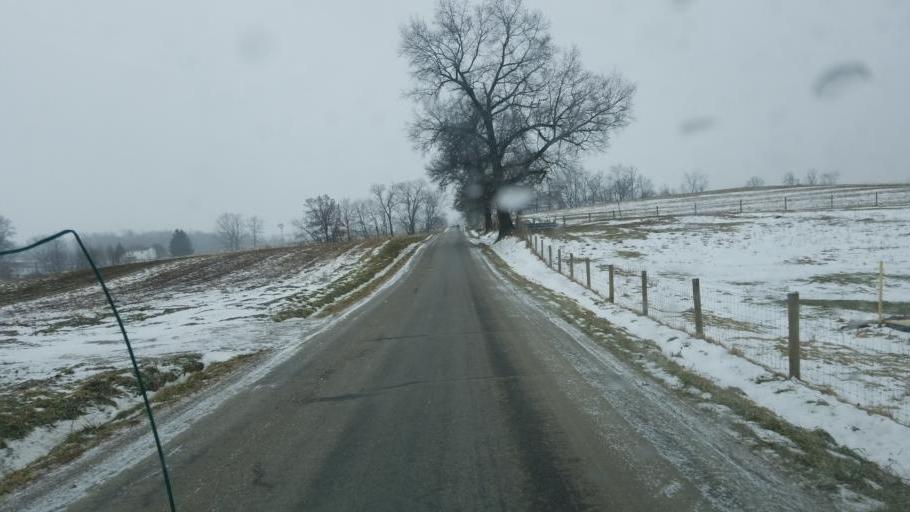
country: US
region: Ohio
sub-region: Wayne County
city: Apple Creek
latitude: 40.6781
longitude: -81.8422
